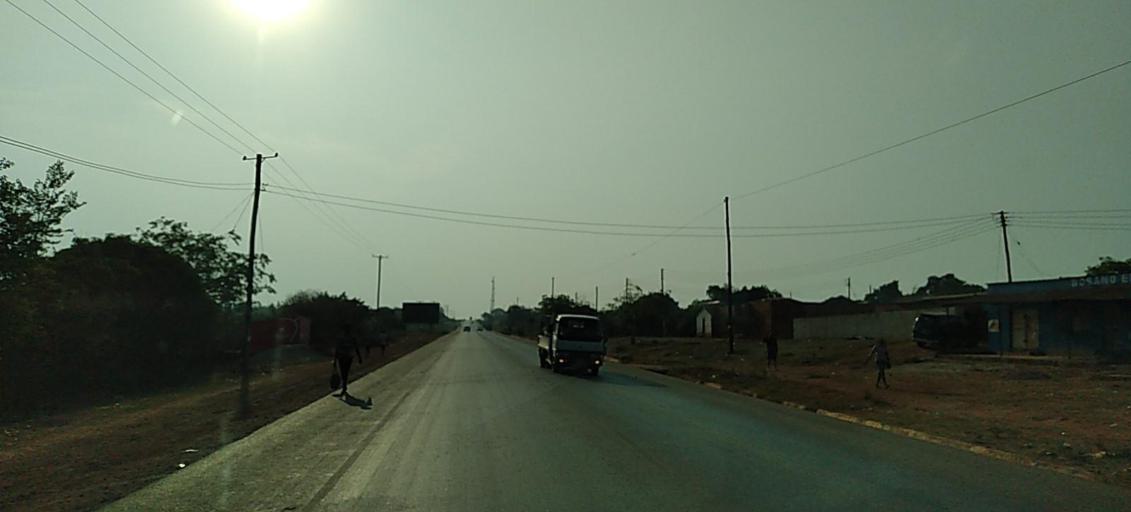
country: ZM
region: North-Western
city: Solwezi
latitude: -12.1897
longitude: 26.4351
